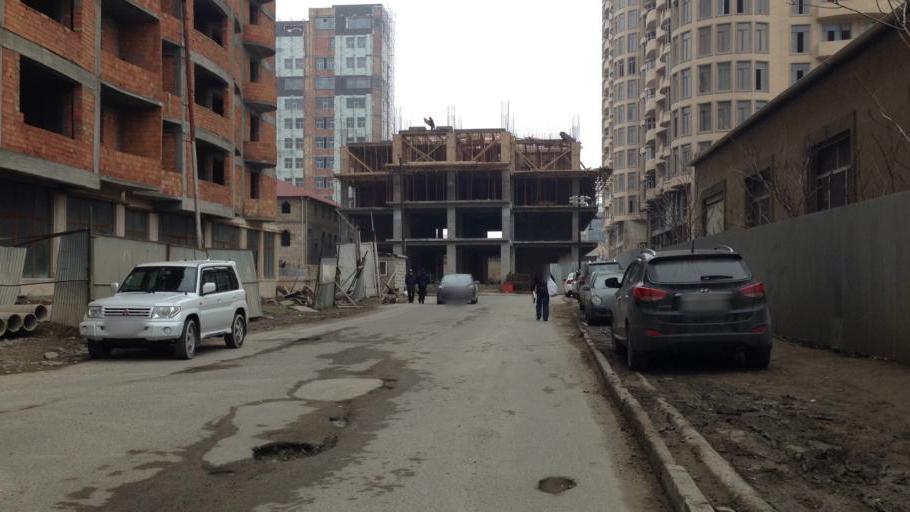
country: AZ
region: Baki
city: Baku
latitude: 40.3839
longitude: 49.8692
